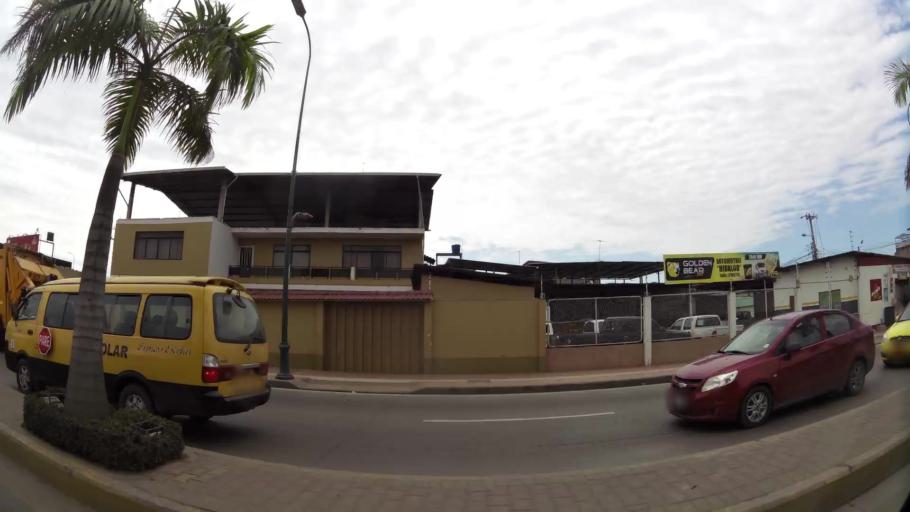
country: EC
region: El Oro
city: Machala
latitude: -3.2685
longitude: -79.9459
